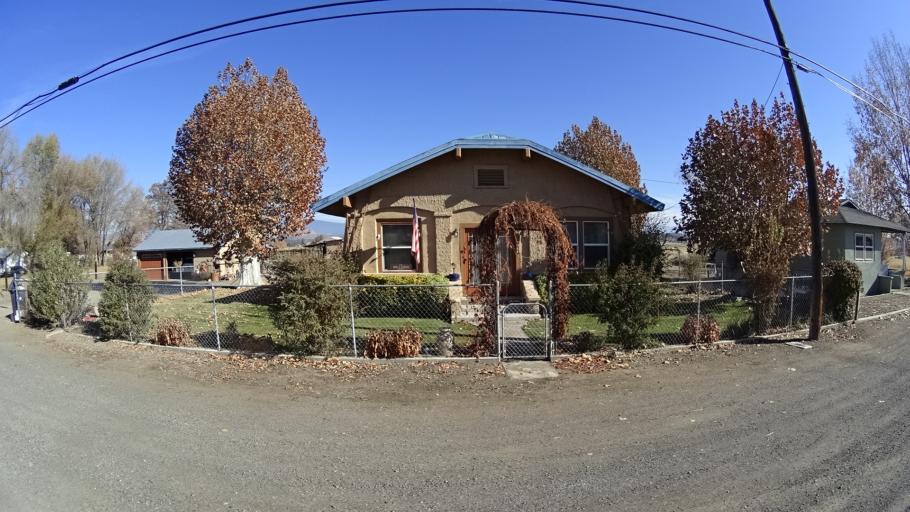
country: US
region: California
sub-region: Siskiyou County
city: Montague
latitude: 41.6406
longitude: -122.5224
